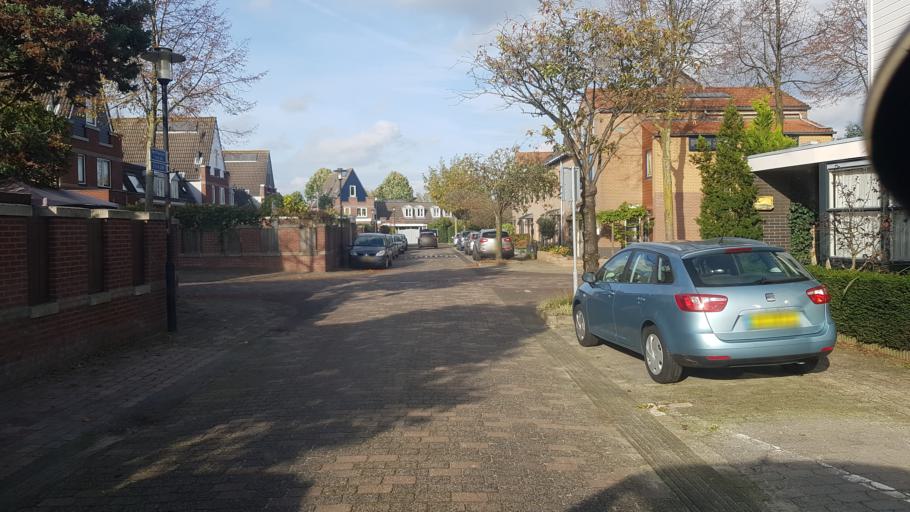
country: NL
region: Gelderland
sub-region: Gemeente Apeldoorn
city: Apeldoorn
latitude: 52.2135
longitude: 6.0090
